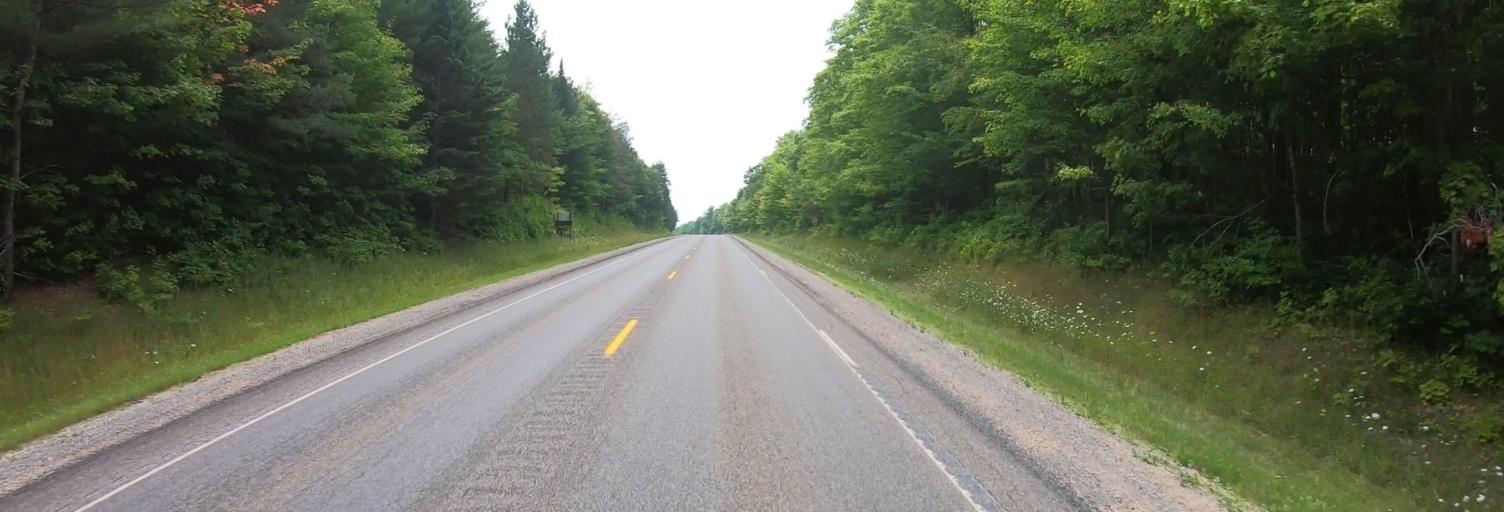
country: US
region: Michigan
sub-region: Alger County
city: Munising
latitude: 46.3582
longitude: -86.7187
